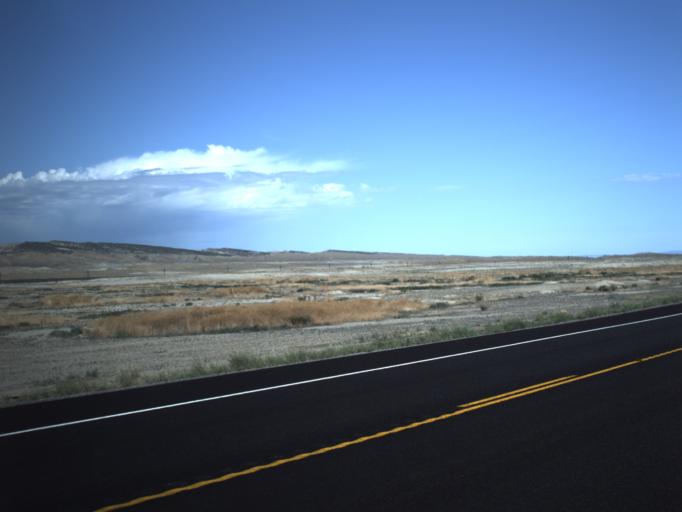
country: US
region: Utah
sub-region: Carbon County
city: East Carbon City
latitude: 39.1621
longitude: -110.3382
